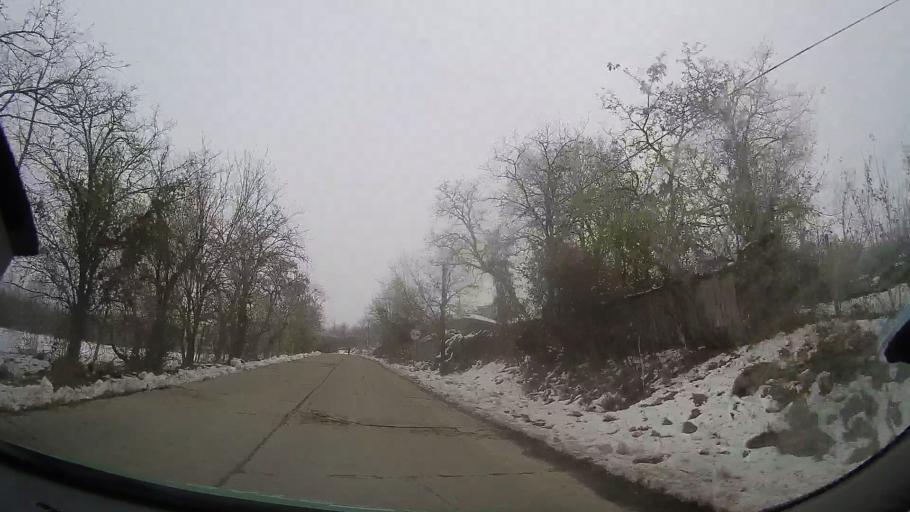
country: RO
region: Vrancea
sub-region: Comuna Boghesti
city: Boghesti
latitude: 46.2056
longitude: 27.4412
